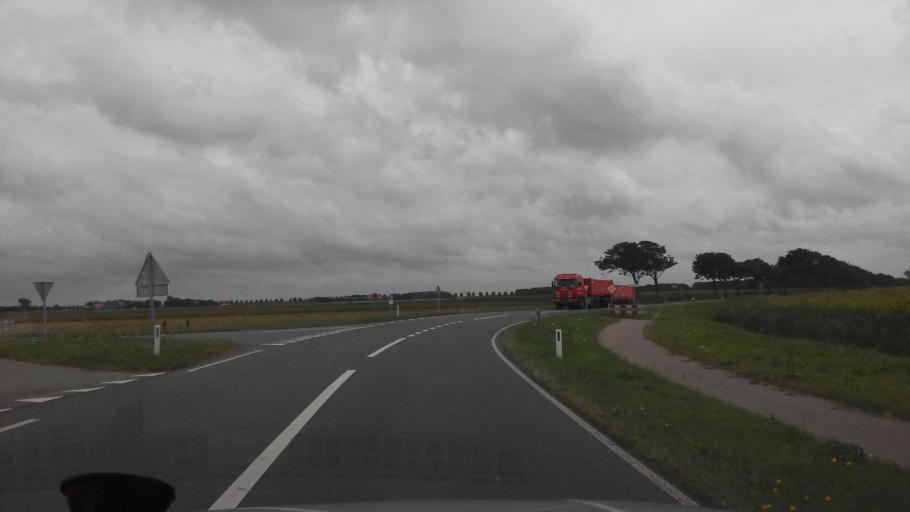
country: NL
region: North Holland
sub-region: Gemeente Hollands Kroon
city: Den Oever
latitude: 52.8879
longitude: 4.9389
